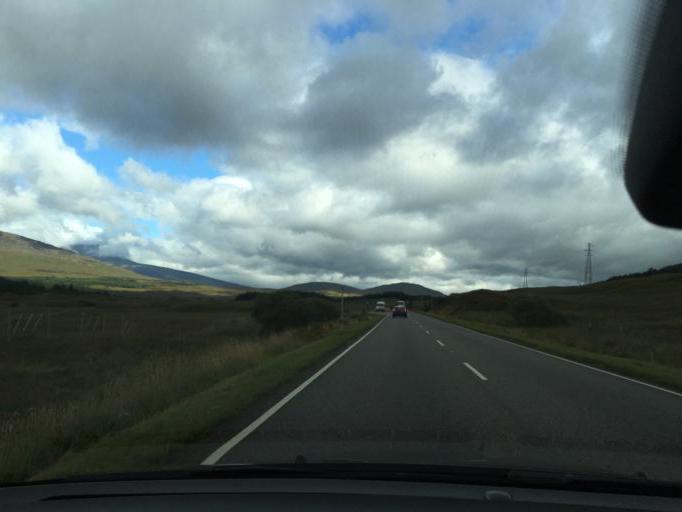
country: GB
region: Scotland
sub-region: Highland
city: Spean Bridge
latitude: 56.5272
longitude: -4.7669
